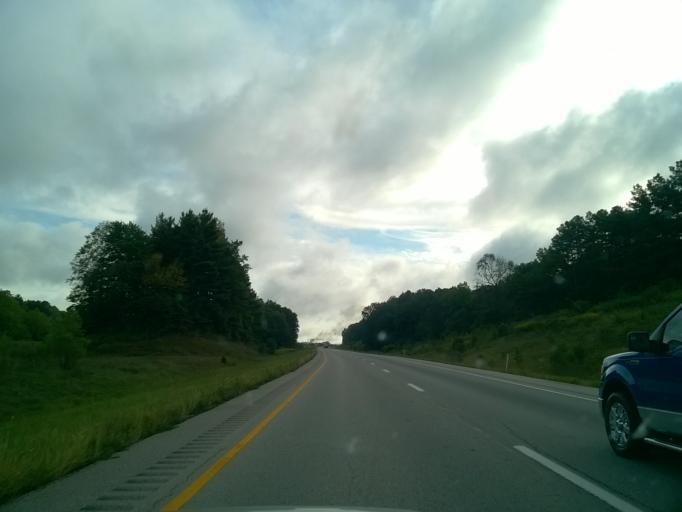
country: US
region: Indiana
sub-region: Dubois County
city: Ferdinand
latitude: 38.2312
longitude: -86.6793
